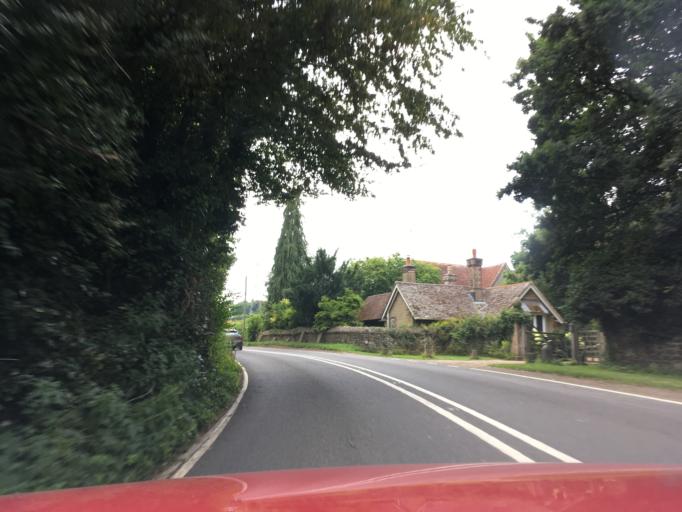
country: GB
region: England
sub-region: West Sussex
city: Milland
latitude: 50.9958
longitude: -0.8106
